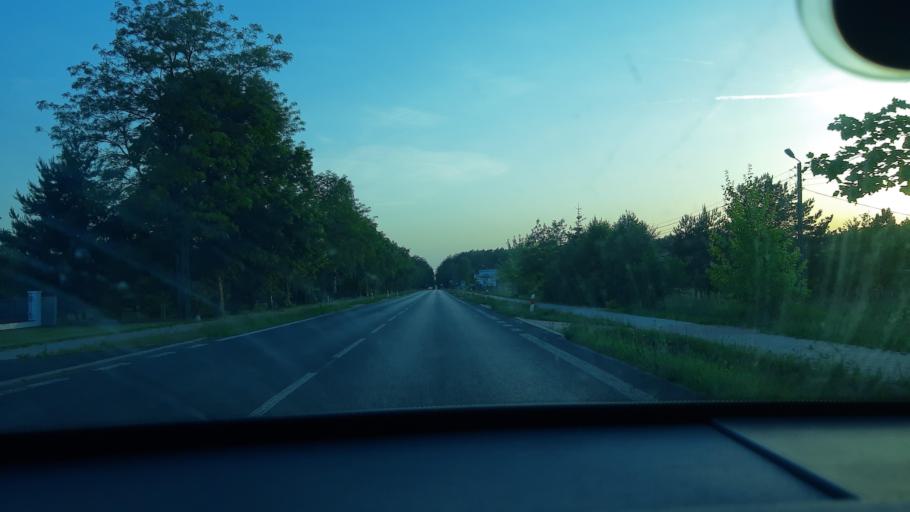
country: PL
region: Lodz Voivodeship
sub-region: Powiat zdunskowolski
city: Zapolice
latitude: 51.6047
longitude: 18.8416
